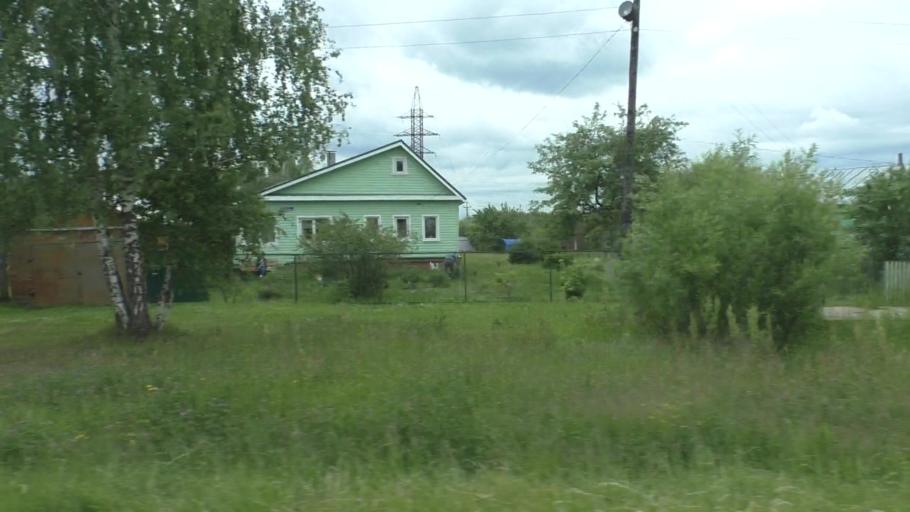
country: RU
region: Moskovskaya
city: Yegor'yevsk
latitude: 55.3977
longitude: 39.0133
